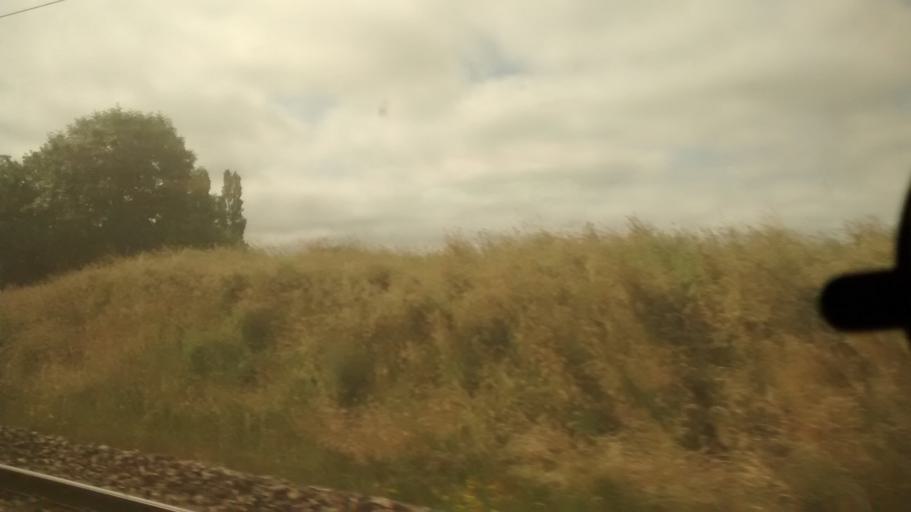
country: FR
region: Centre
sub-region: Departement d'Eure-et-Loir
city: La Bazoche-Gouet
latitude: 48.0764
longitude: 0.9574
